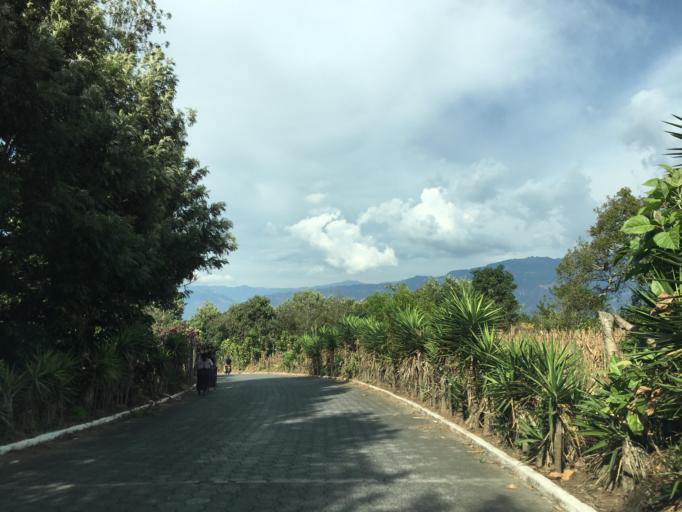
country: GT
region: Solola
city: San Antonio Palopo
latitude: 14.6565
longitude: -91.1583
